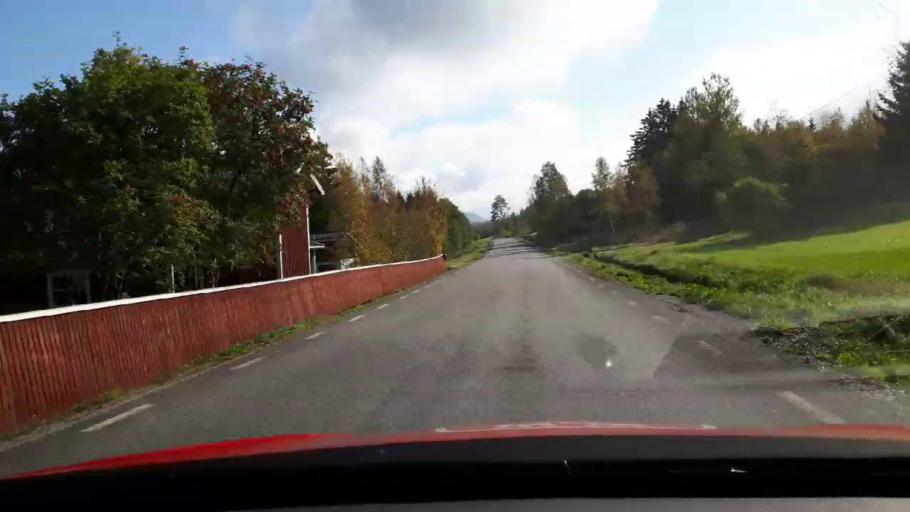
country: SE
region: Gaevleborg
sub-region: Ljusdals Kommun
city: Ljusdal
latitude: 61.7585
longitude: 16.1007
